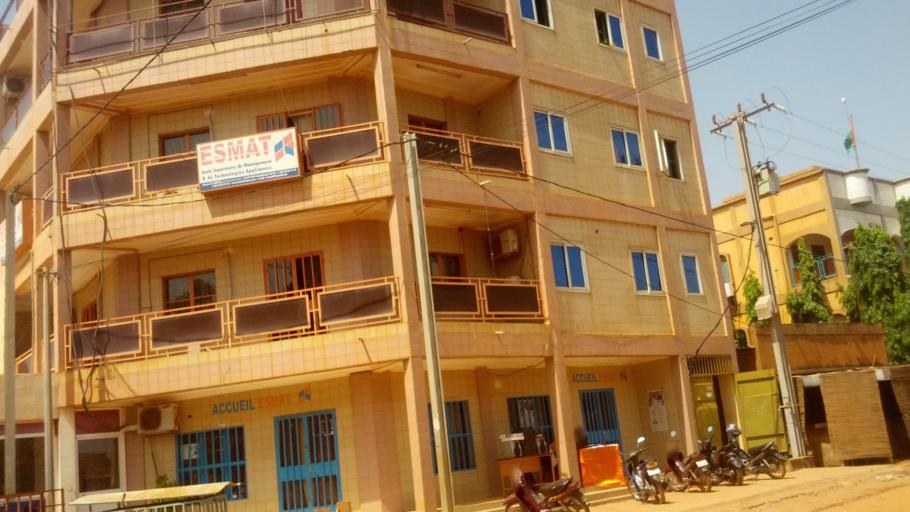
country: BF
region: Centre
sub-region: Kadiogo Province
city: Ouagadougou
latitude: 12.3851
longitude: -1.4681
